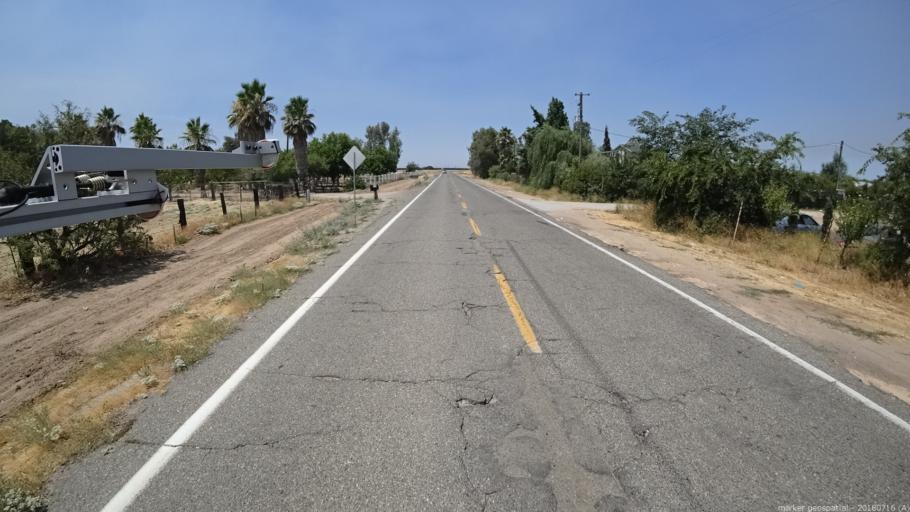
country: US
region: California
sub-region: Madera County
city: Madera Acres
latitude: 37.0536
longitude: -120.0911
